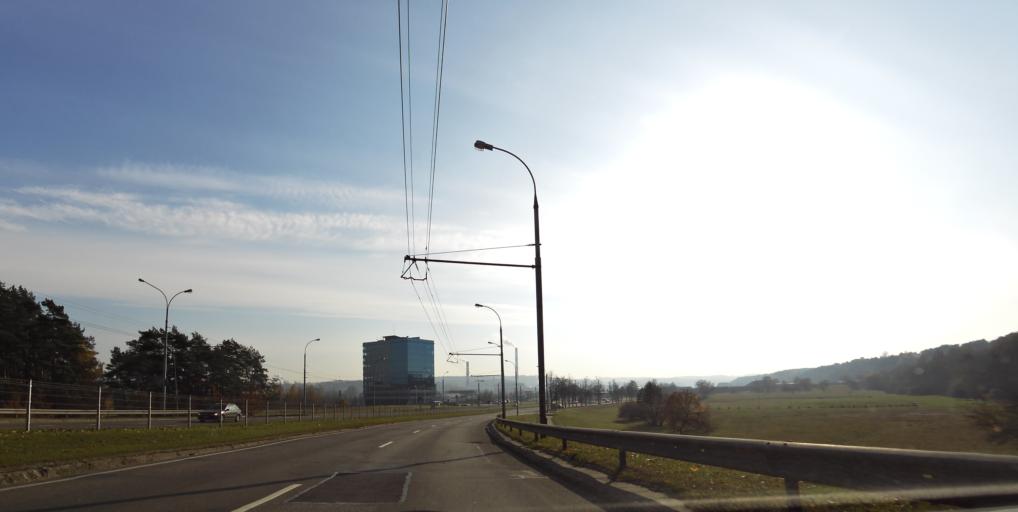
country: LT
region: Vilnius County
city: Lazdynai
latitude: 54.6769
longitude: 25.2206
